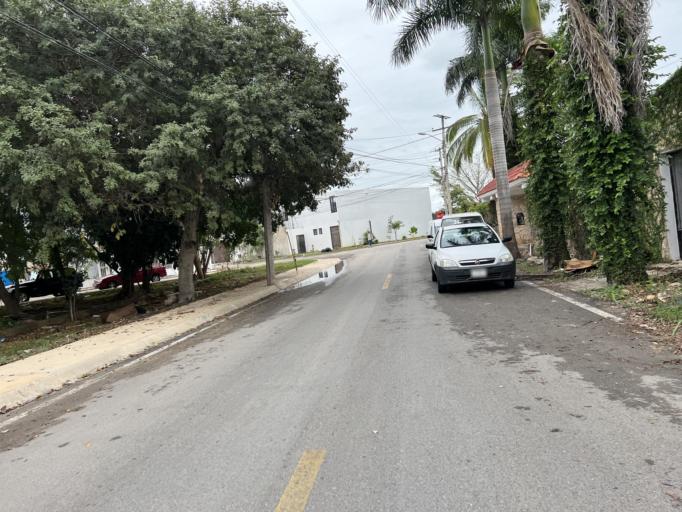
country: MX
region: Yucatan
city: Merida
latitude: 20.9965
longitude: -89.5854
